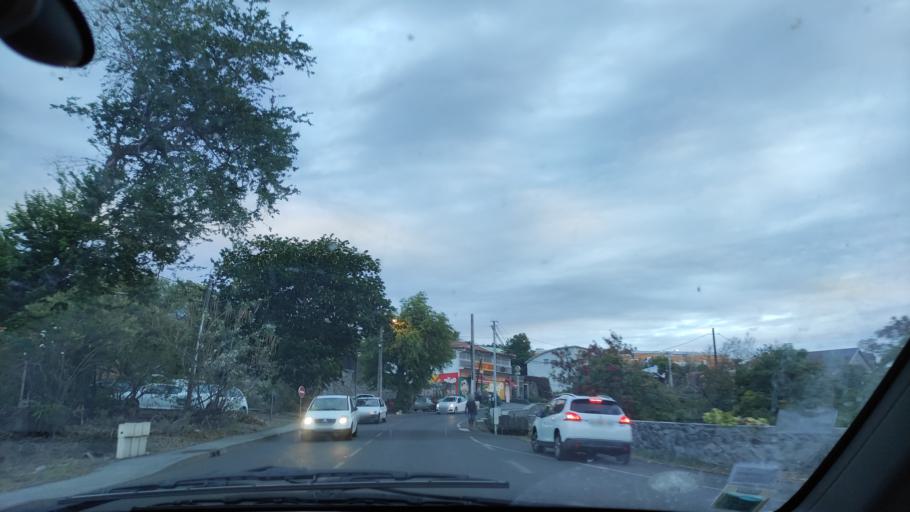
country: RE
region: Reunion
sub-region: Reunion
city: Saint-Leu
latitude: -21.1968
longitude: 55.2922
